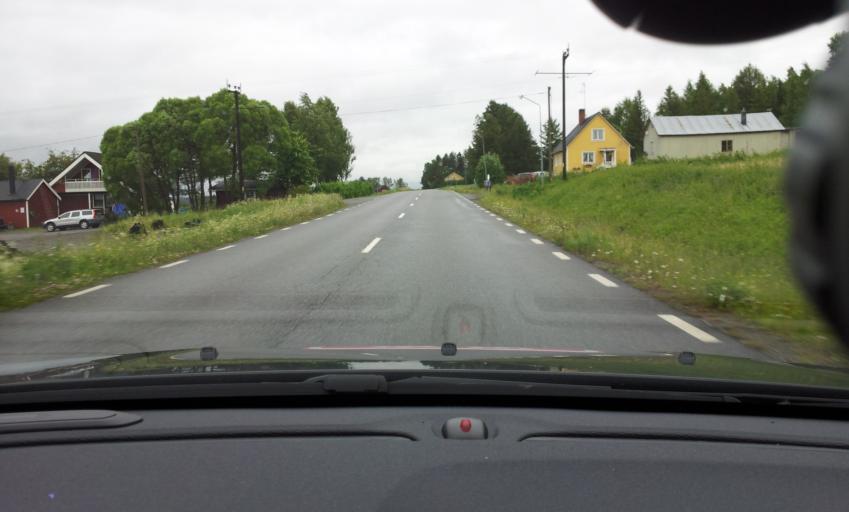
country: SE
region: Jaemtland
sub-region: Stroemsunds Kommun
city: Stroemsund
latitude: 63.5641
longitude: 15.3952
